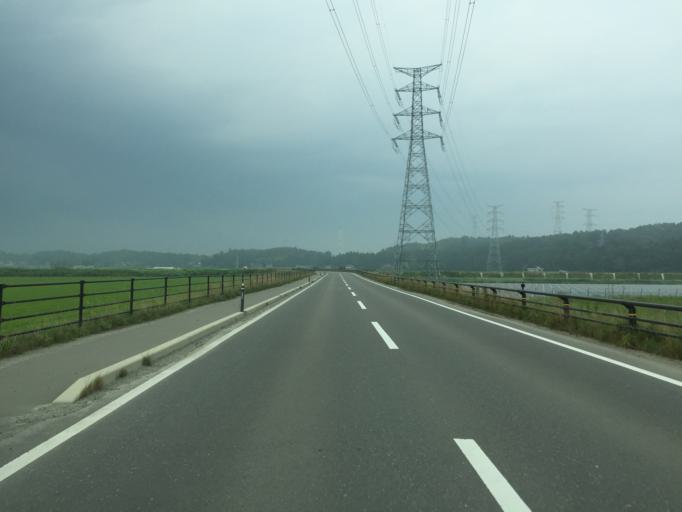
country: JP
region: Fukushima
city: Namie
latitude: 37.6392
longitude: 141.0163
